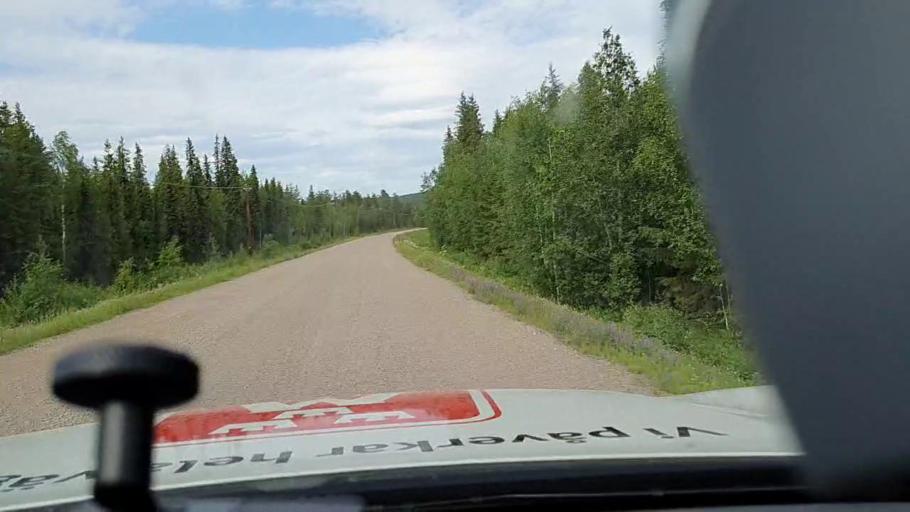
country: SE
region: Norrbotten
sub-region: Alvsbyns Kommun
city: AElvsbyn
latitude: 66.1168
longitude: 20.9763
